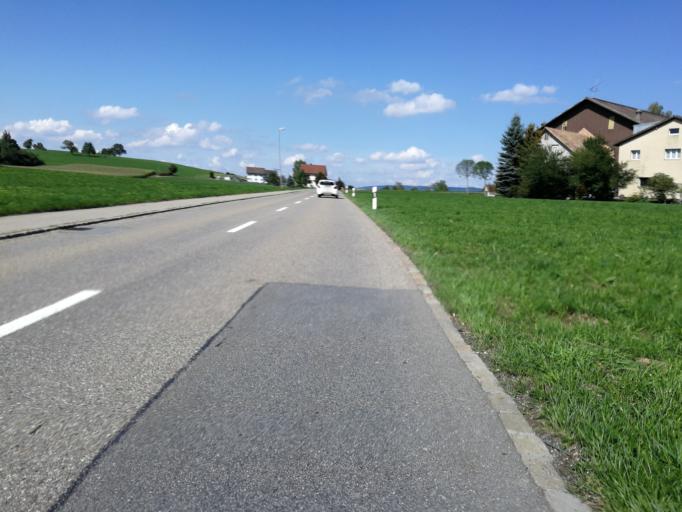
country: CH
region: Zurich
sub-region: Bezirk Horgen
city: Waedenswil / Eichweid
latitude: 47.2104
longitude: 8.6646
